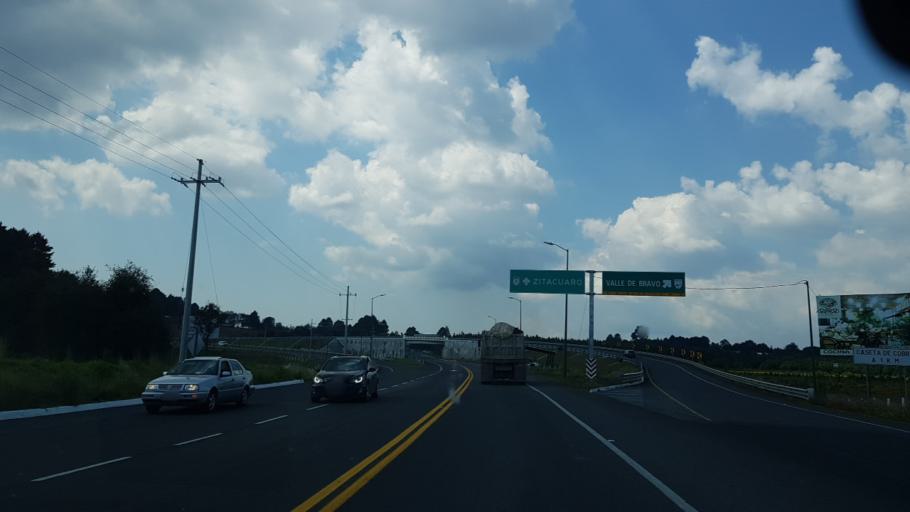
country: MX
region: Mexico
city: Amanalco de Becerra
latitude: 19.3547
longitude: -99.9833
